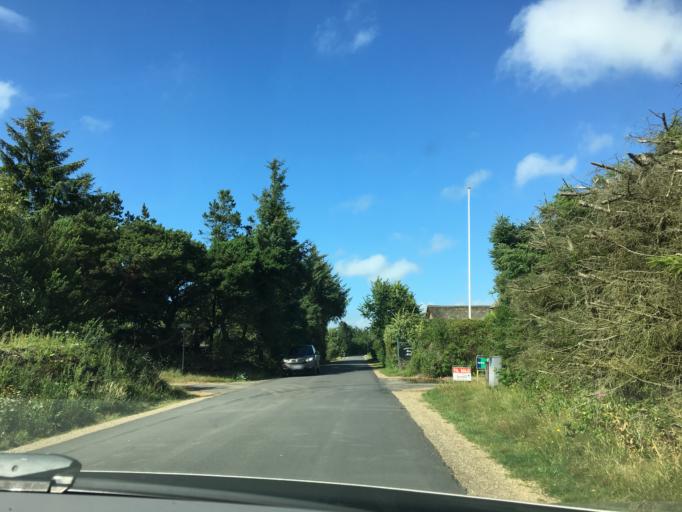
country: DK
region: South Denmark
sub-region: Varde Kommune
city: Oksbol
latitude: 55.7351
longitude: 8.2225
